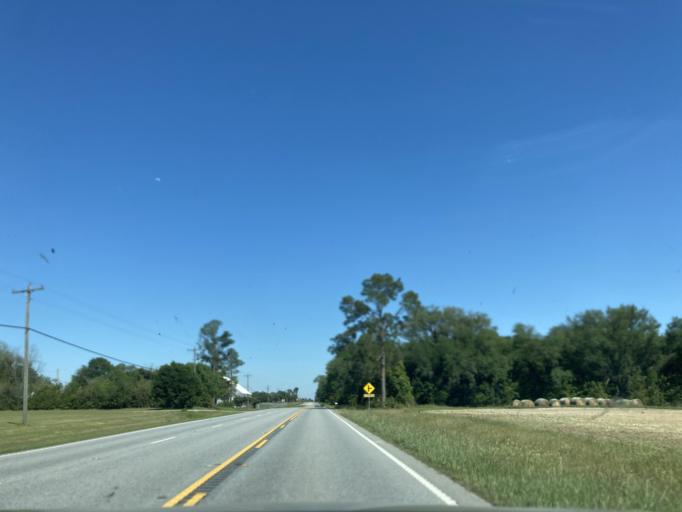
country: US
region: Georgia
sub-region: Miller County
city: Colquitt
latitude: 31.1855
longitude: -84.6070
